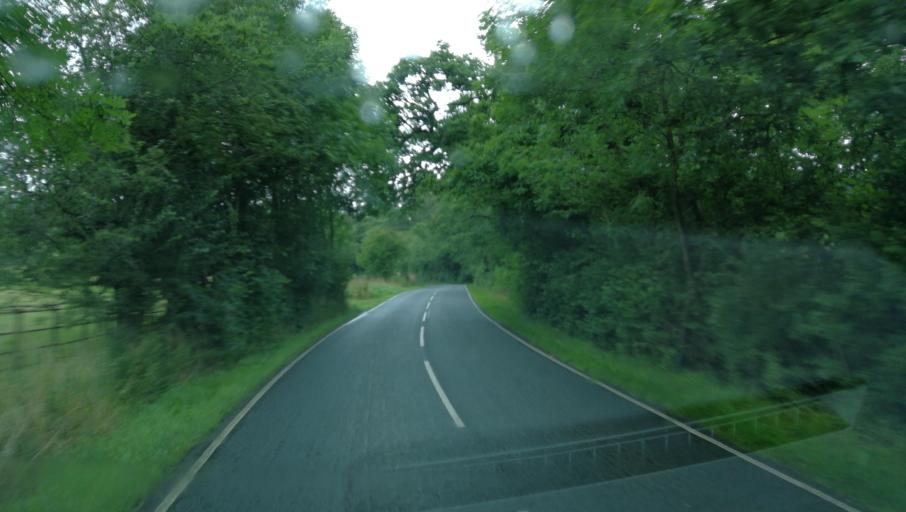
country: GB
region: England
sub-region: Cumbria
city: Penrith
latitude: 54.6276
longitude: -2.8122
